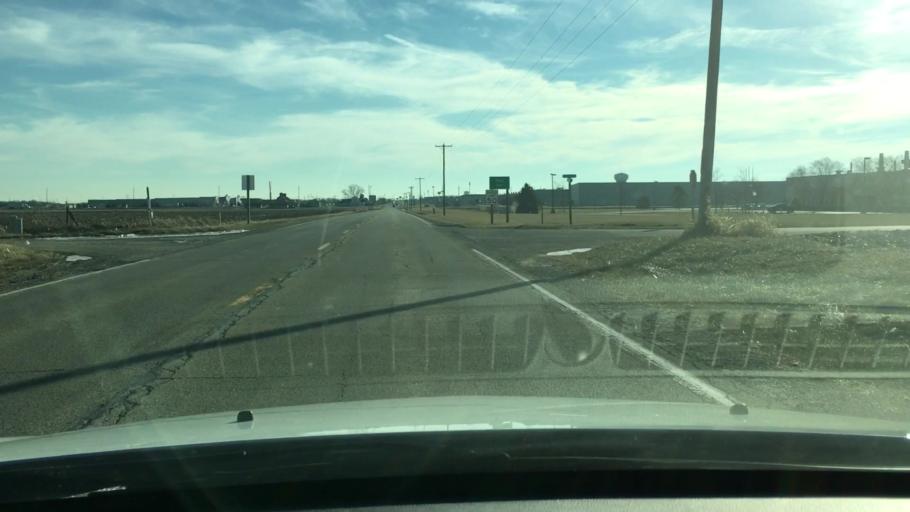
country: US
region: Illinois
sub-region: LaSalle County
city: Peru
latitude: 41.3822
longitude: -89.1257
